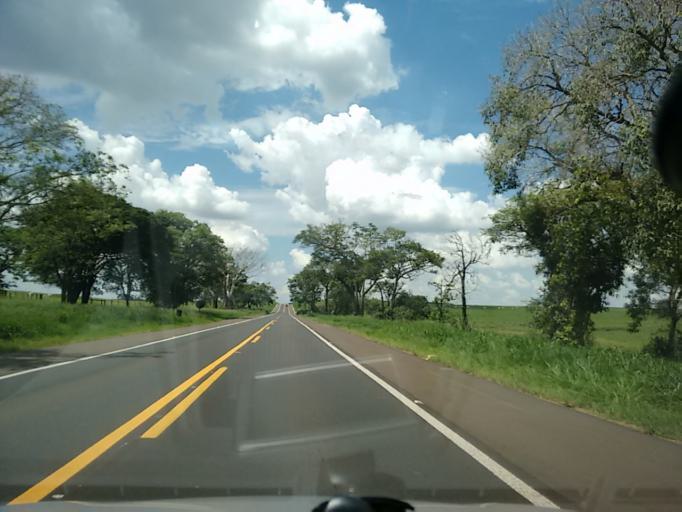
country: BR
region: Sao Paulo
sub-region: Osvaldo Cruz
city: Osvaldo Cruz
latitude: -21.8758
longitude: -50.8597
